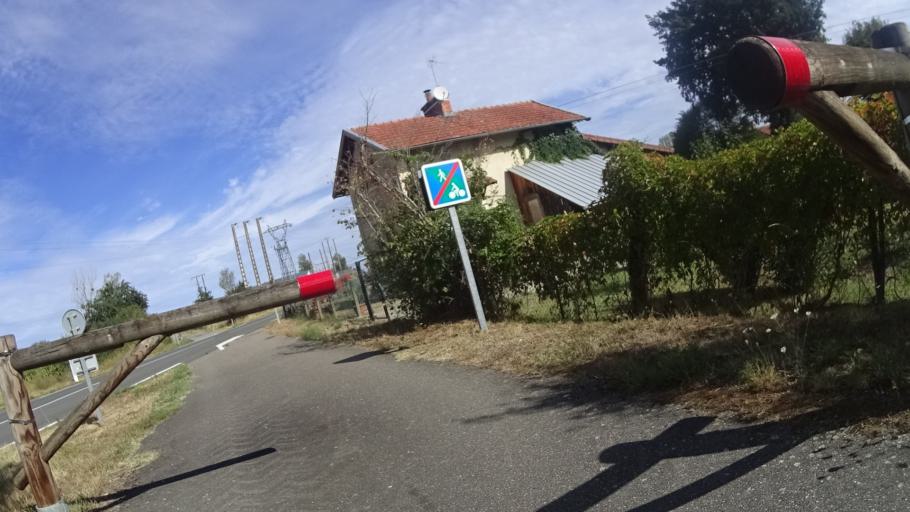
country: FR
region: Bourgogne
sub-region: Departement de Saone-et-Loire
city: Bourbon-Lancy
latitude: 46.6203
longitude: 3.7396
